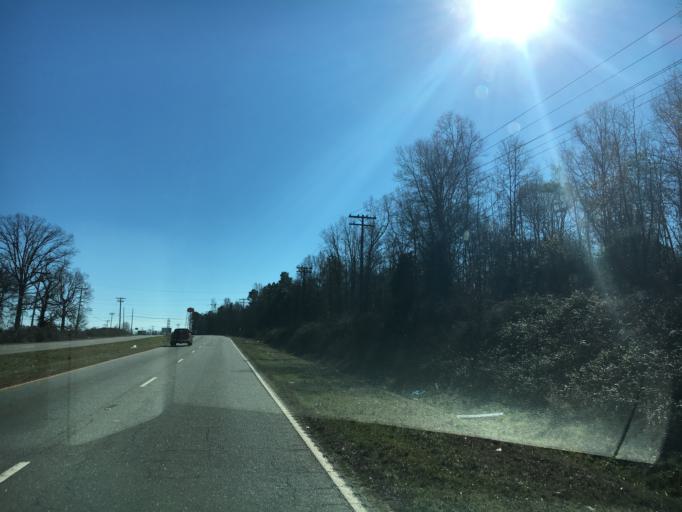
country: US
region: South Carolina
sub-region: Anderson County
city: Homeland Park
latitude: 34.4454
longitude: -82.6680
